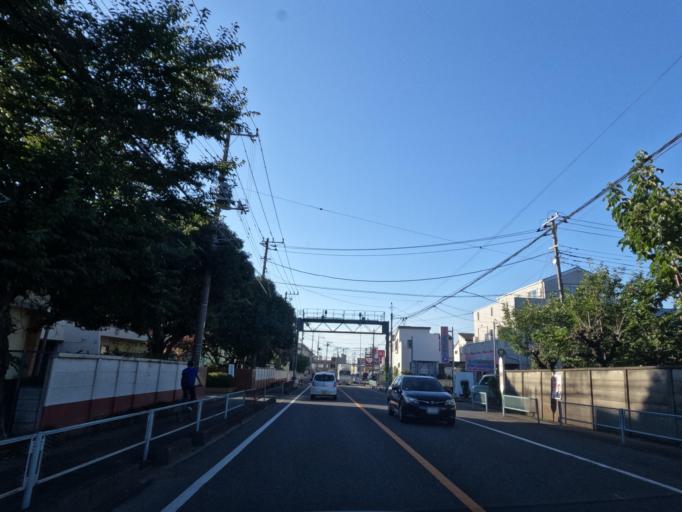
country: JP
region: Saitama
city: Shimotoda
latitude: 35.8564
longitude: 139.6787
